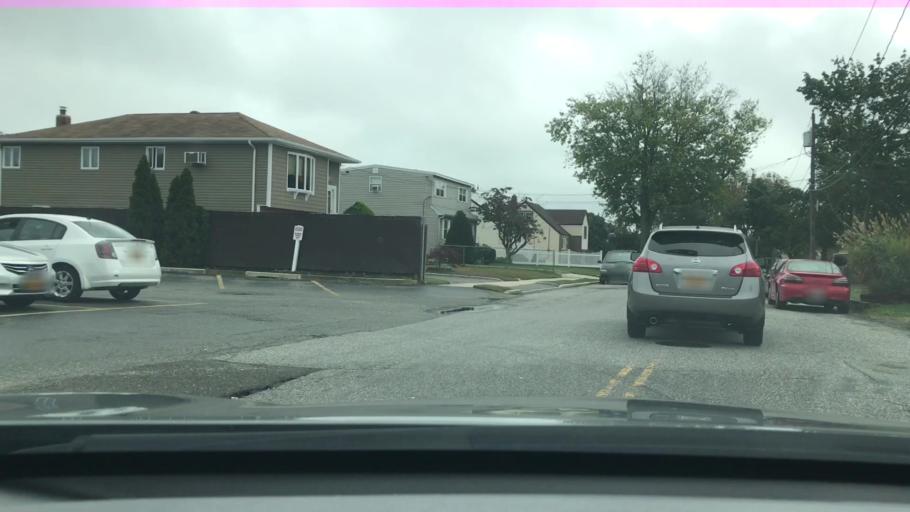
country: US
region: New York
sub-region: Suffolk County
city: Lindenhurst
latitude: 40.6742
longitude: -73.3731
